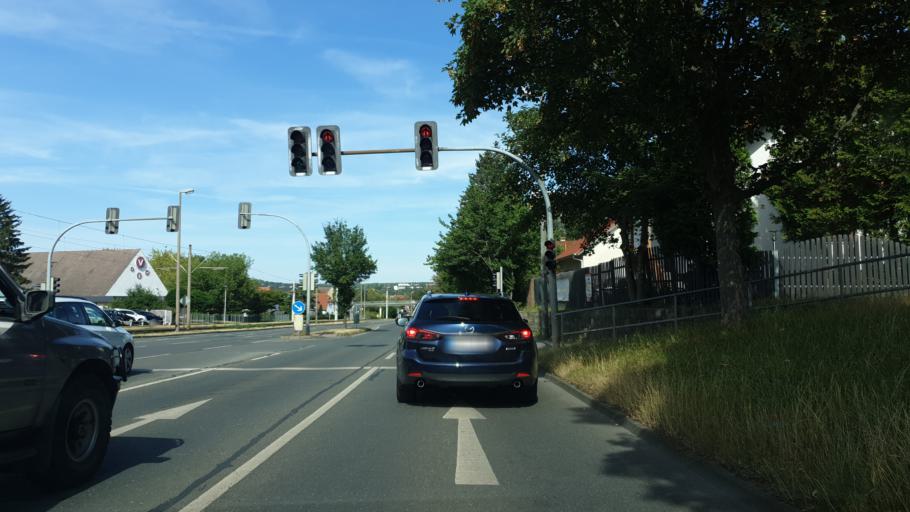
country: DE
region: Thuringia
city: Gera
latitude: 50.8476
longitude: 12.0680
